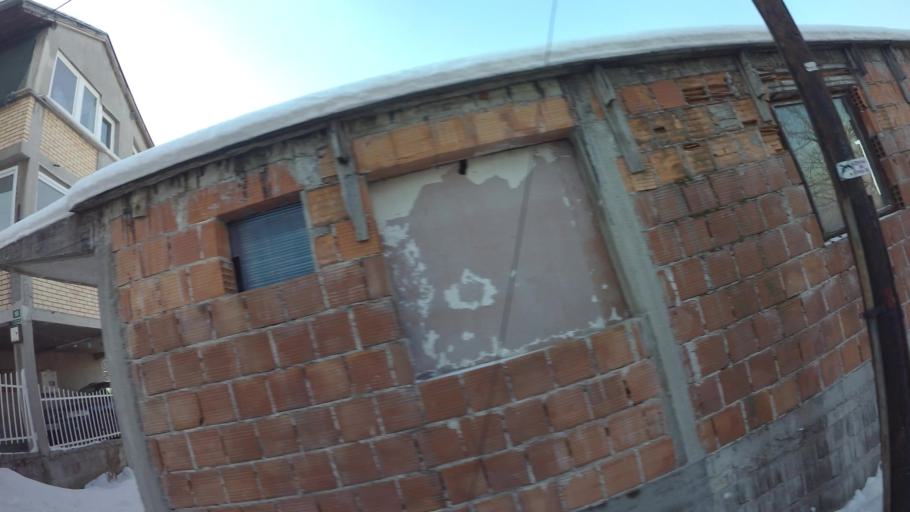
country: BA
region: Federation of Bosnia and Herzegovina
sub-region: Kanton Sarajevo
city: Sarajevo
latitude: 43.8408
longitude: 18.3631
